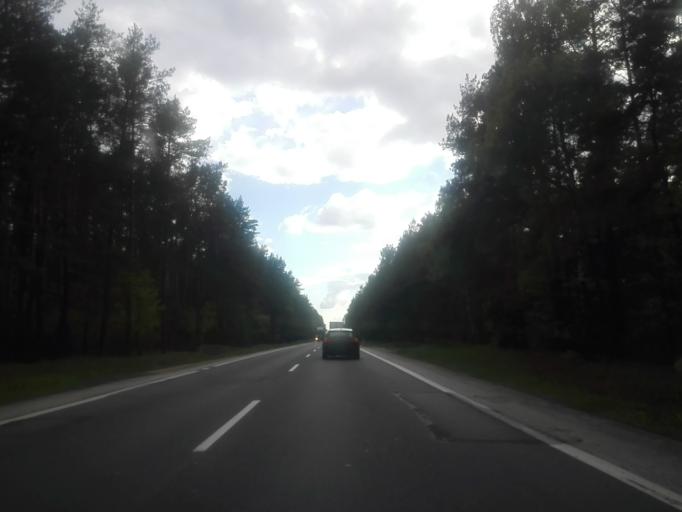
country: PL
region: Masovian Voivodeship
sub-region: Powiat ostrowski
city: Brok
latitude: 52.7325
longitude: 21.7386
